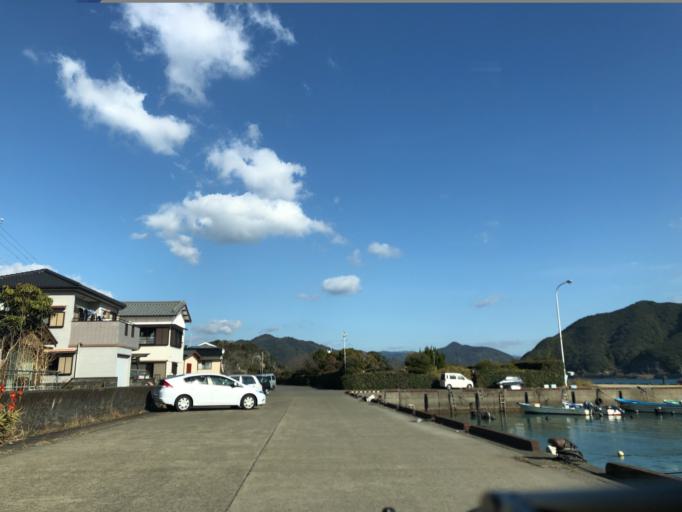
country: JP
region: Kochi
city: Sukumo
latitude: 32.9148
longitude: 132.7043
